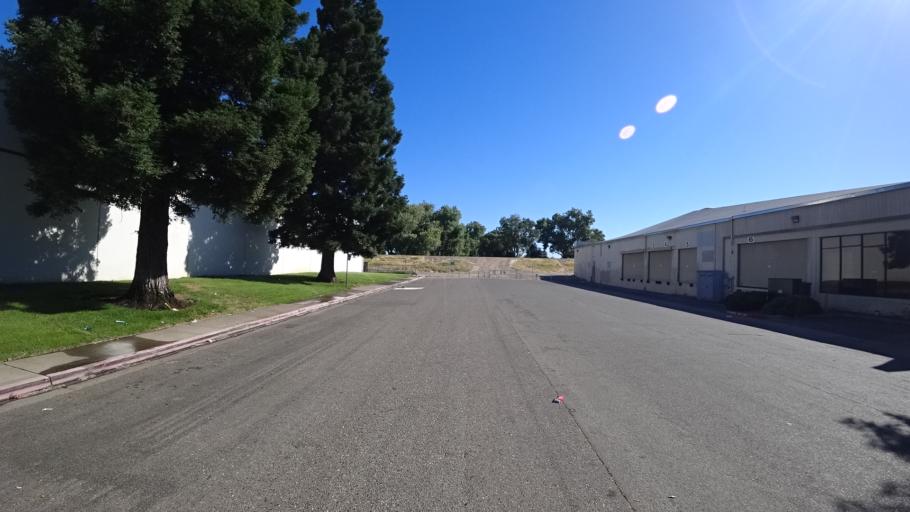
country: US
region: California
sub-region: Sacramento County
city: Sacramento
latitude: 38.5999
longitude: -121.4851
